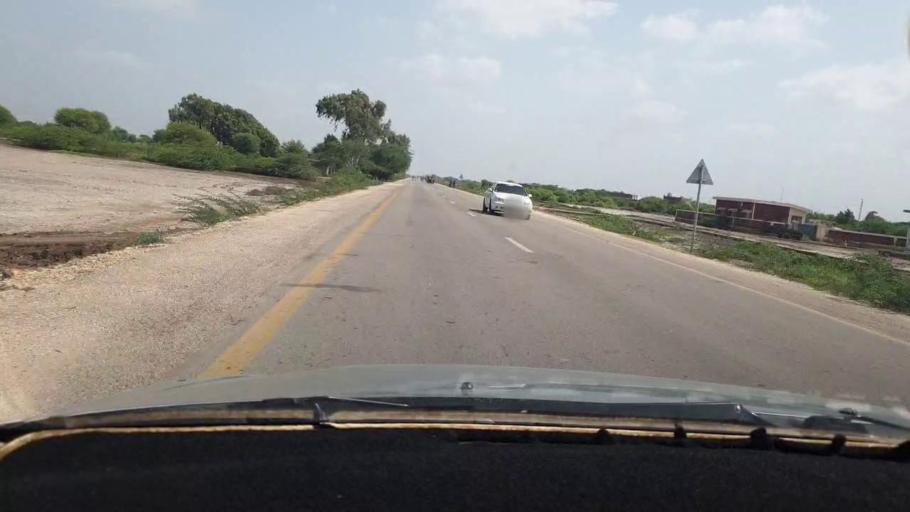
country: PK
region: Sindh
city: Digri
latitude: 25.1289
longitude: 69.1413
